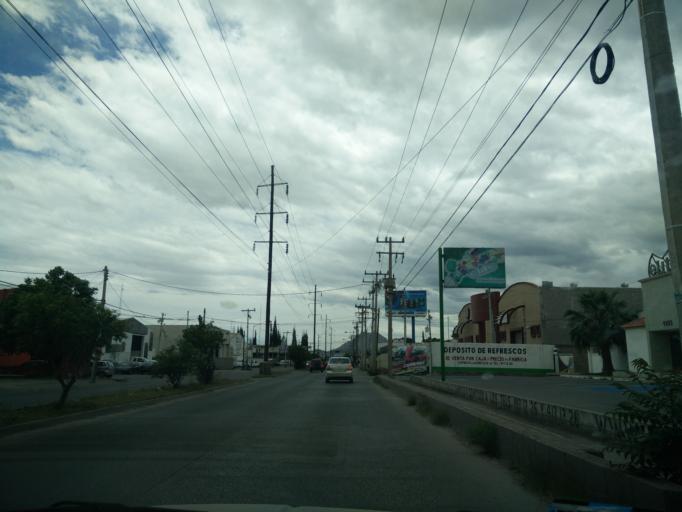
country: MX
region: Chihuahua
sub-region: Chihuahua
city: Chihuahua
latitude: 28.6704
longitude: -106.0855
